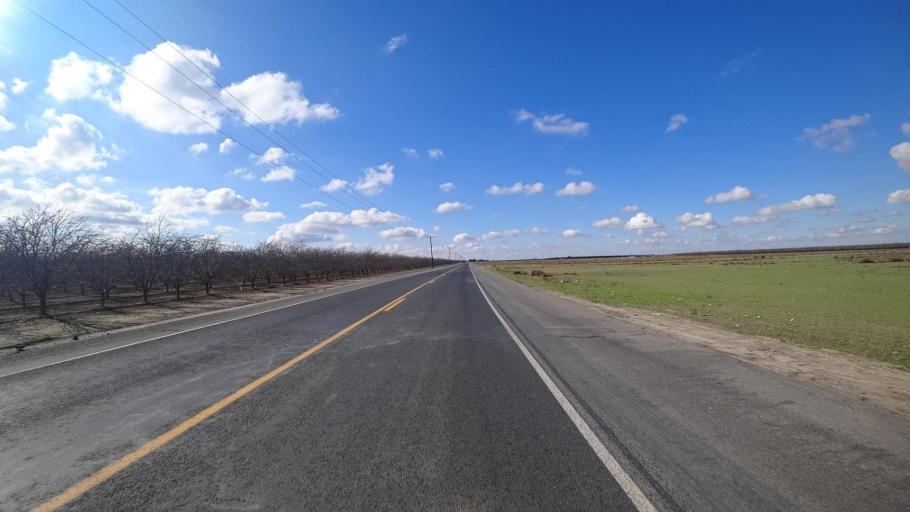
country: US
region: California
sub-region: Kern County
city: McFarland
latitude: 35.7179
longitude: -119.2417
